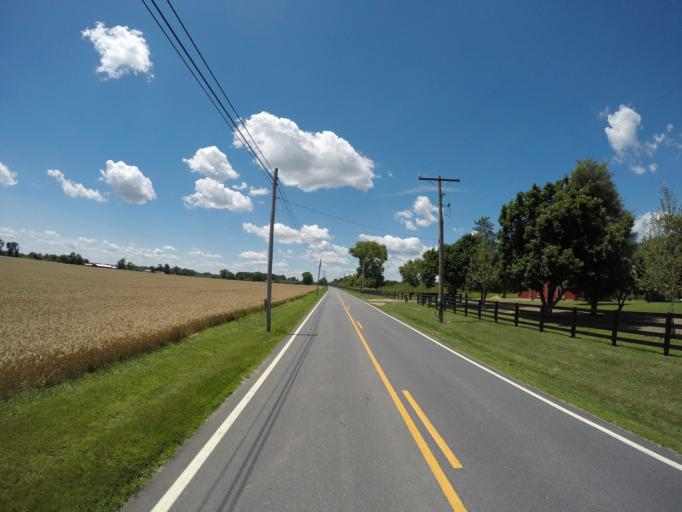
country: US
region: Delaware
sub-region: New Castle County
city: Middletown
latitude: 39.4611
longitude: -75.7529
